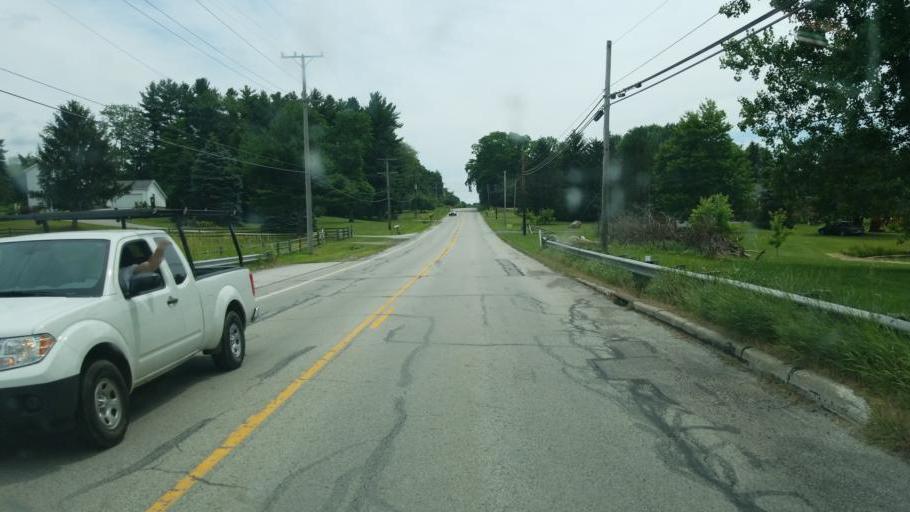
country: US
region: Ohio
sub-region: Geauga County
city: Bainbridge
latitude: 41.3881
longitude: -81.2687
